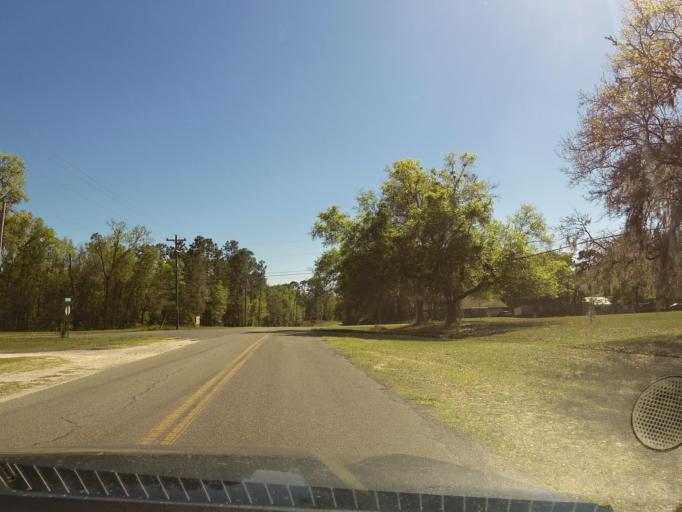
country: US
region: Florida
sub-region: Clay County
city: Keystone Heights
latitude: 29.8174
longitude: -82.0577
